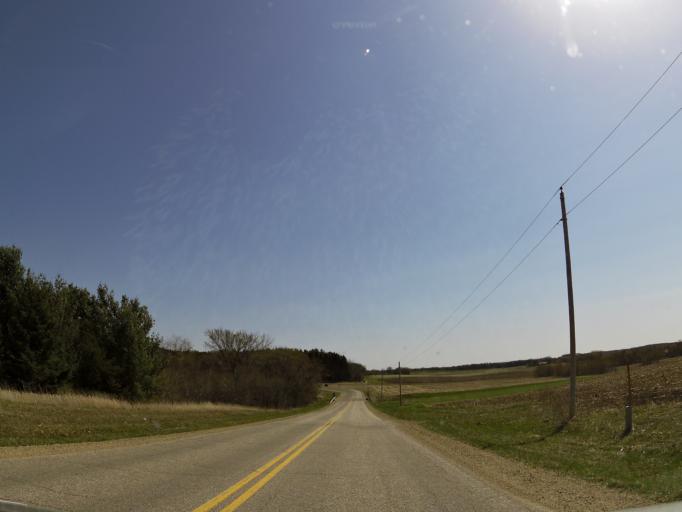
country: US
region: Wisconsin
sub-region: Saint Croix County
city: Baldwin
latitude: 44.8582
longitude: -92.4155
